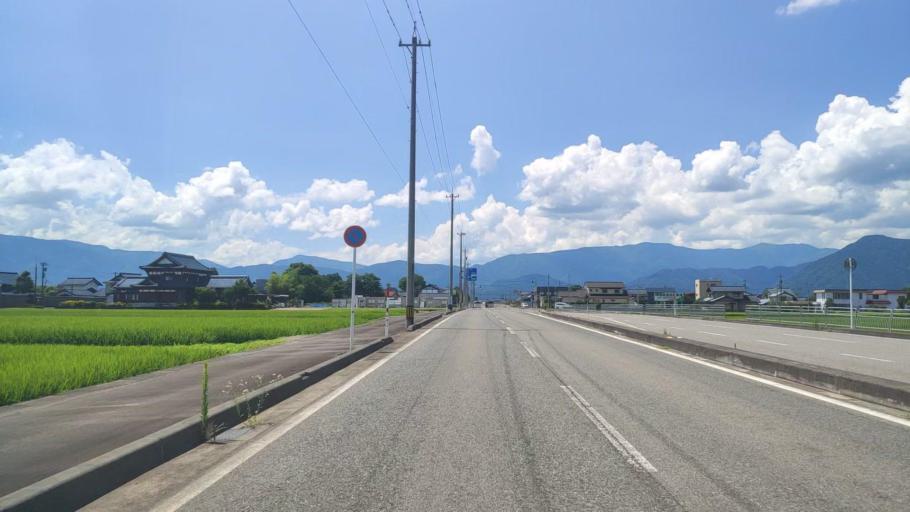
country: JP
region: Fukui
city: Ono
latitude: 36.0053
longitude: 136.5092
